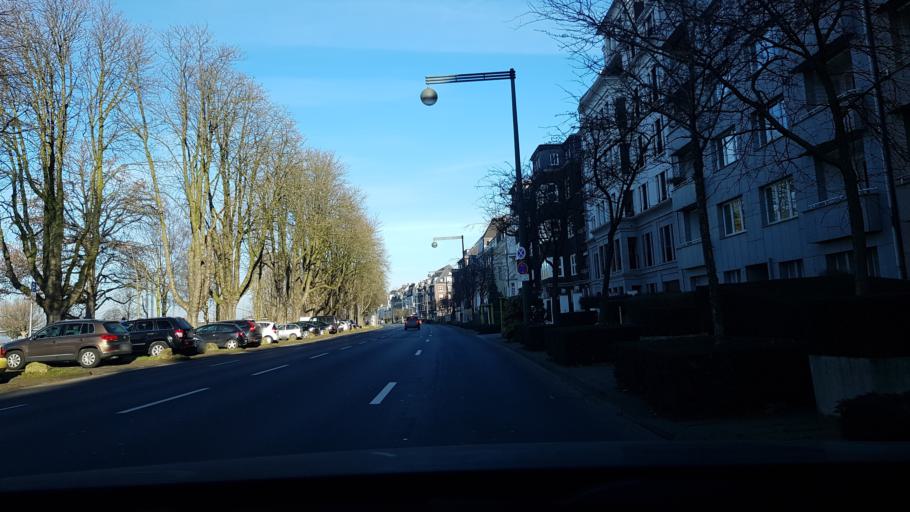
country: DE
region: North Rhine-Westphalia
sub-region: Regierungsbezirk Dusseldorf
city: Dusseldorf
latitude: 51.2441
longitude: 6.7690
